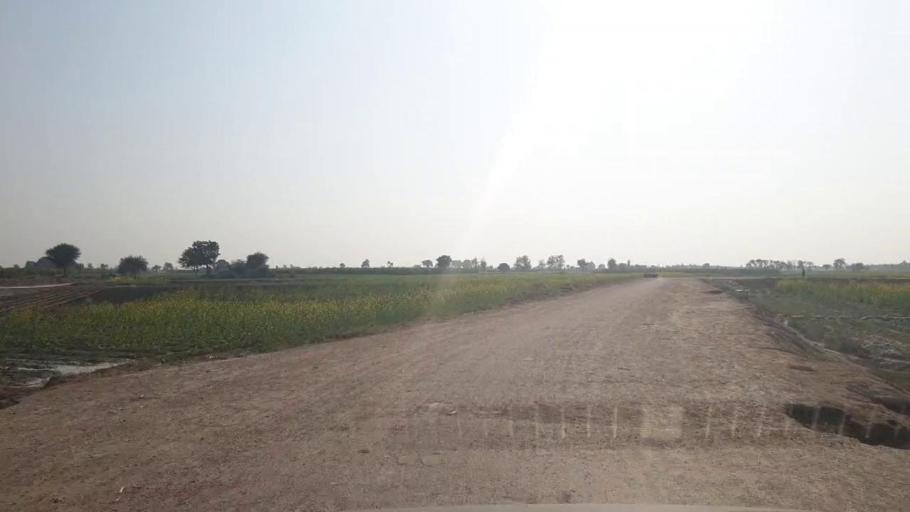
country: PK
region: Sindh
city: Bhit Shah
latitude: 25.8188
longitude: 68.5668
